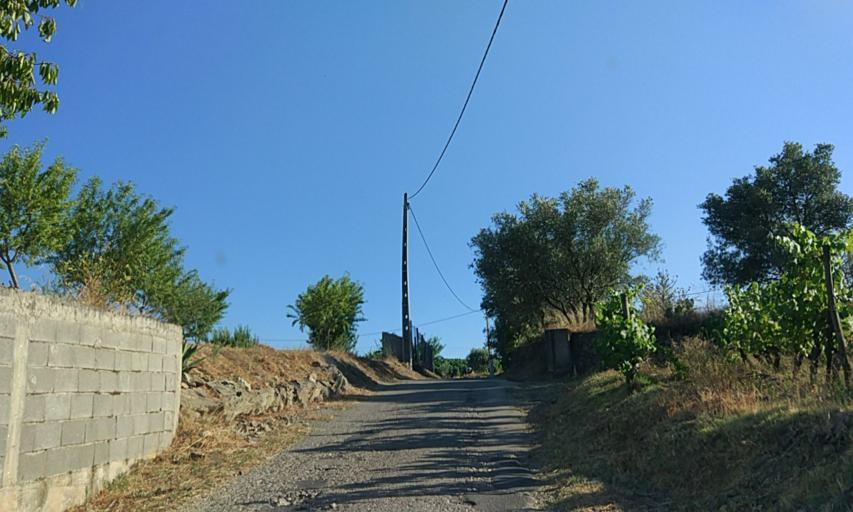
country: PT
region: Viseu
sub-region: Sao Joao da Pesqueira
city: Sao Joao da Pesqueira
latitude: 41.1549
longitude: -7.4204
